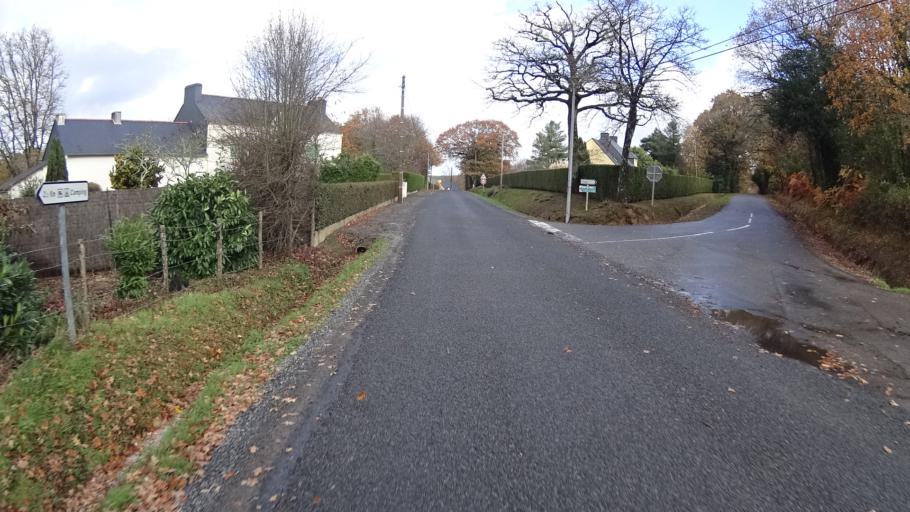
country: FR
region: Pays de la Loire
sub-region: Departement de la Loire-Atlantique
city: Fegreac
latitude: 47.6003
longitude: -2.0668
